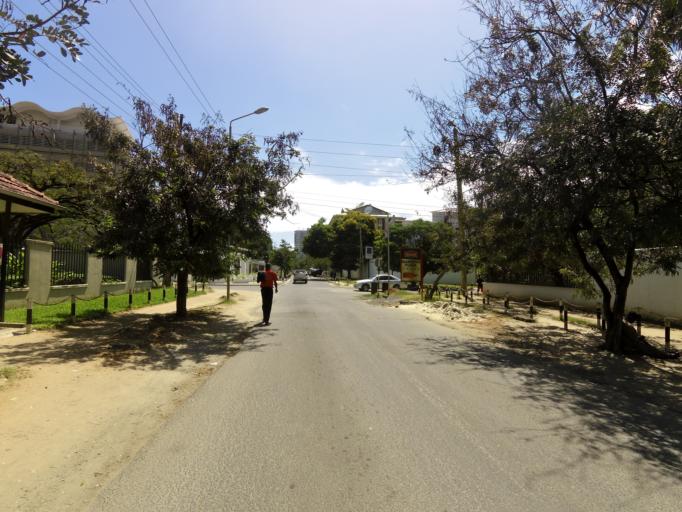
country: TZ
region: Dar es Salaam
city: Dar es Salaam
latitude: -6.8131
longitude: 39.2914
